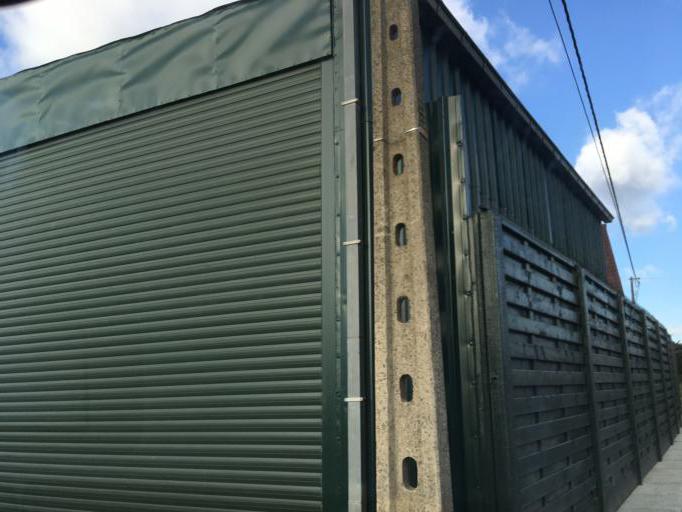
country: BE
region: Flanders
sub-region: Provincie West-Vlaanderen
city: Roeselare
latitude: 50.9595
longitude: 3.1592
